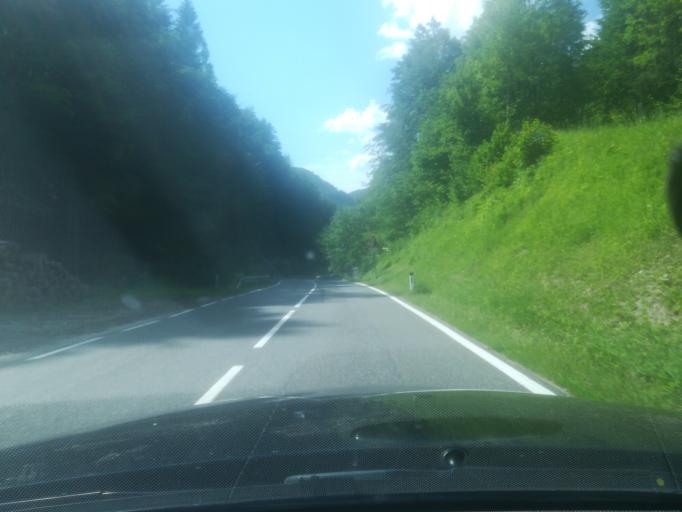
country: AT
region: Styria
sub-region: Politischer Bezirk Liezen
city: Hall
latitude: 47.7090
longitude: 14.4351
